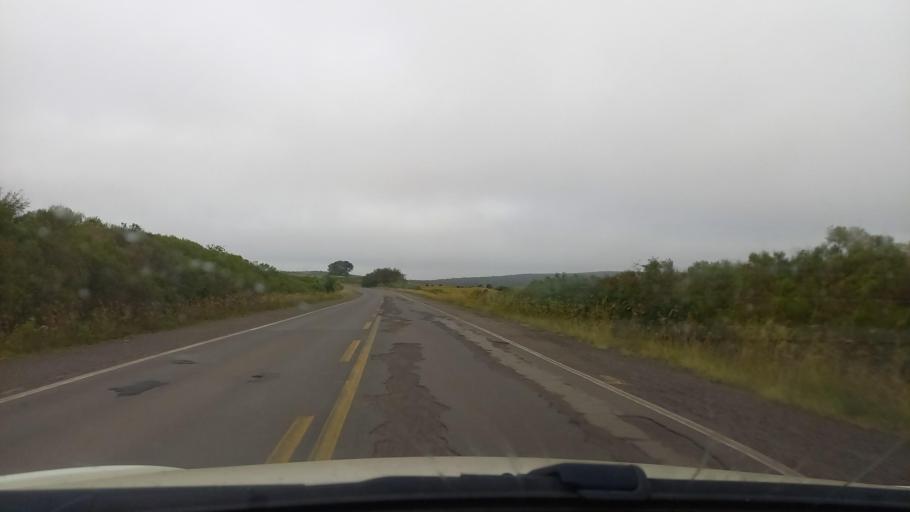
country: BR
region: Rio Grande do Sul
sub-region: Rosario Do Sul
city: Rosario do Sul
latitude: -30.1420
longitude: -54.6701
